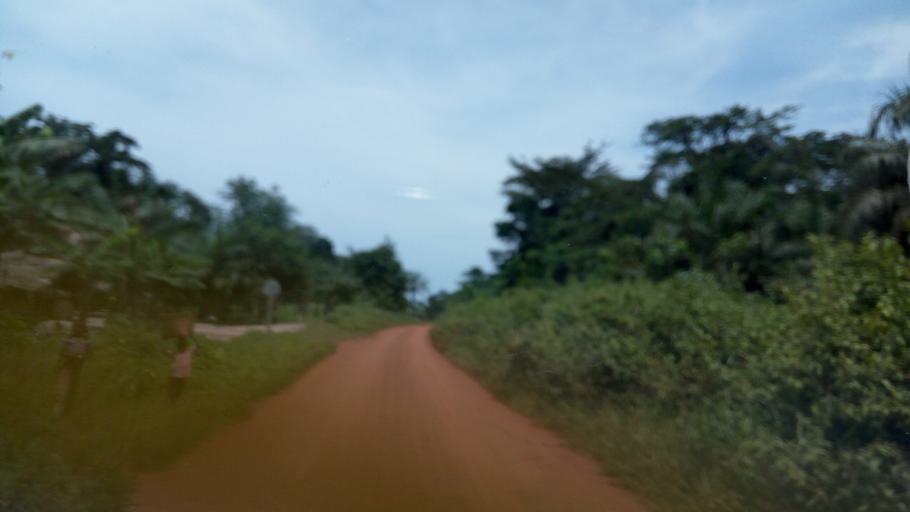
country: CD
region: Equateur
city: Gemena
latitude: 3.3156
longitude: 19.4226
